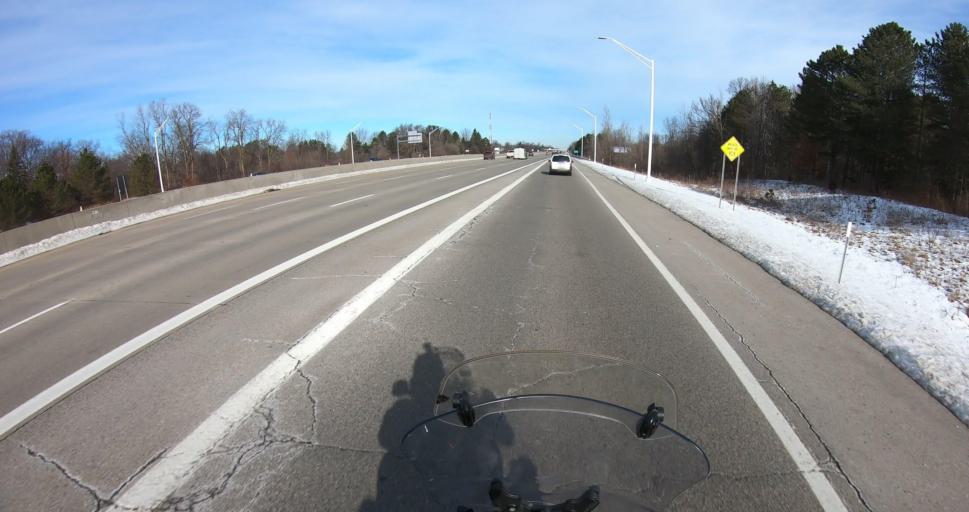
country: US
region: Michigan
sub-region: Genesee County
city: Clio
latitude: 43.1852
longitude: -83.7665
